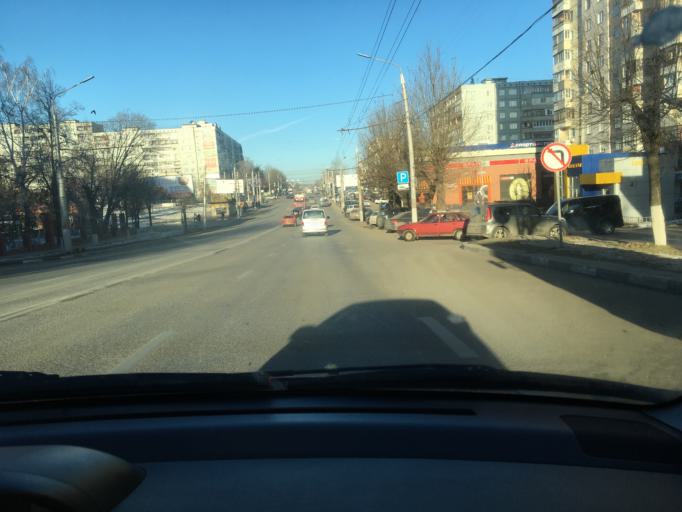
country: RU
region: Tula
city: Tula
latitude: 54.2160
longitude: 37.6240
